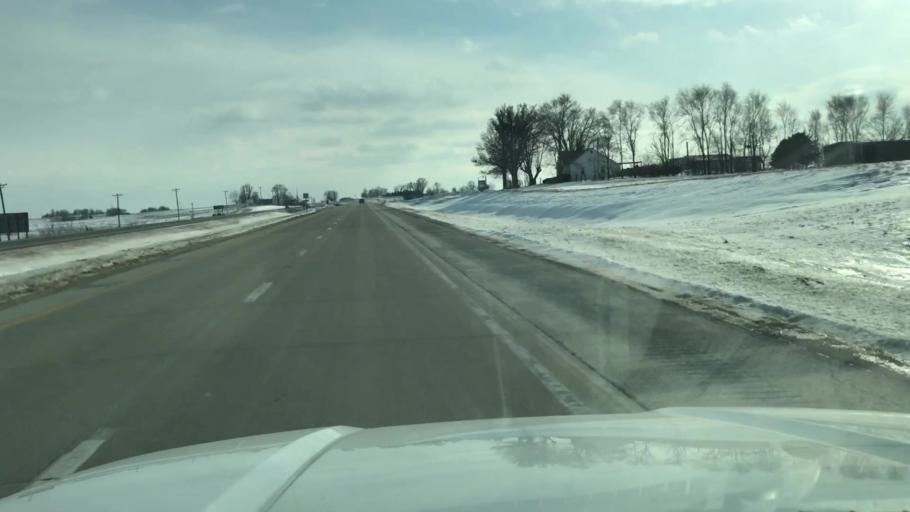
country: US
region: Missouri
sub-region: Nodaway County
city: Maryville
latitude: 40.2898
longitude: -94.8756
